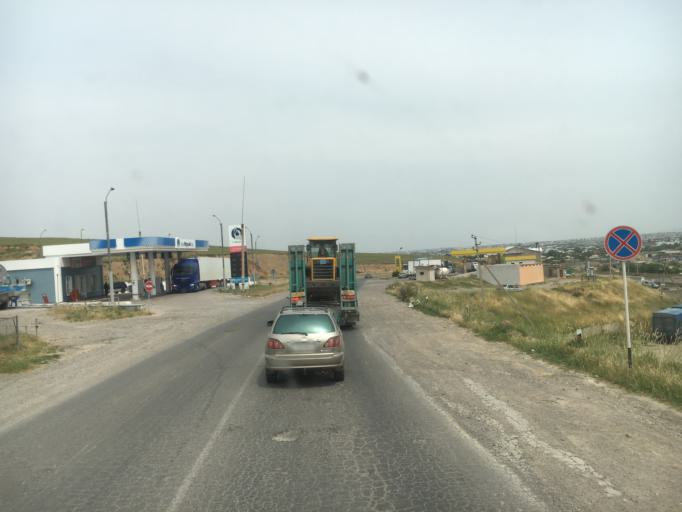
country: KZ
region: Ongtustik Qazaqstan
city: Shymkent
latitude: 42.3268
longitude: 69.5139
